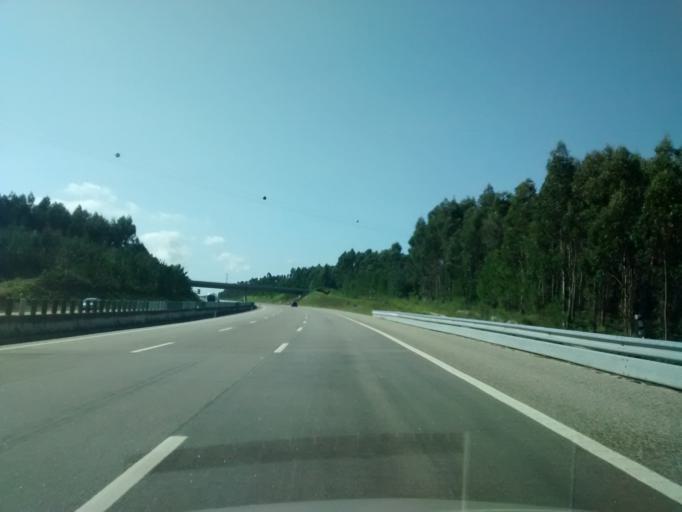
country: PT
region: Leiria
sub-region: Pombal
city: Lourical
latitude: 40.0042
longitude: -8.7994
